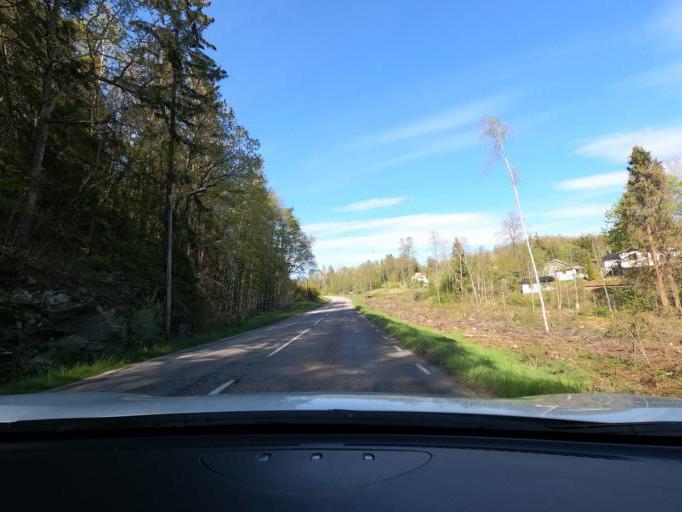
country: SE
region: Vaestra Goetaland
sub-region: Harryda Kommun
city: Landvetter
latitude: 57.6135
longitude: 12.2885
